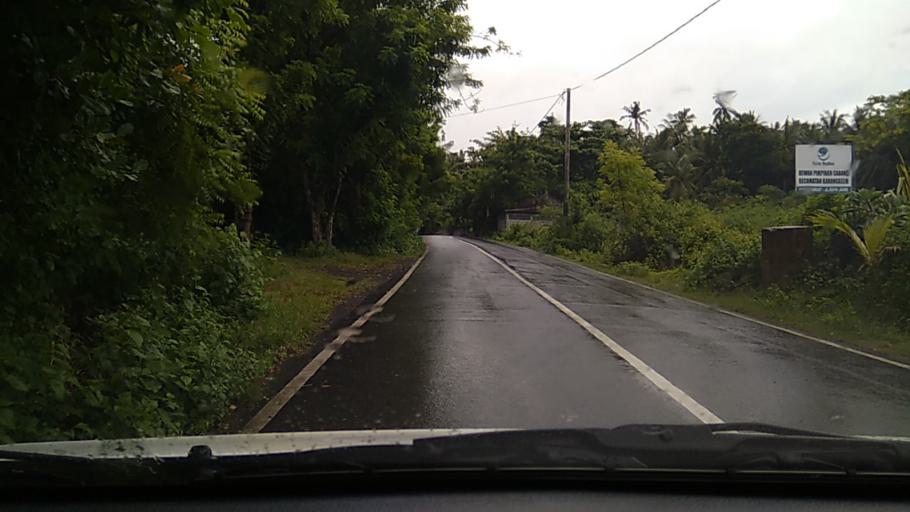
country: ID
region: Bali
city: Banjar Danginsema
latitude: -8.4711
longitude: 115.6211
